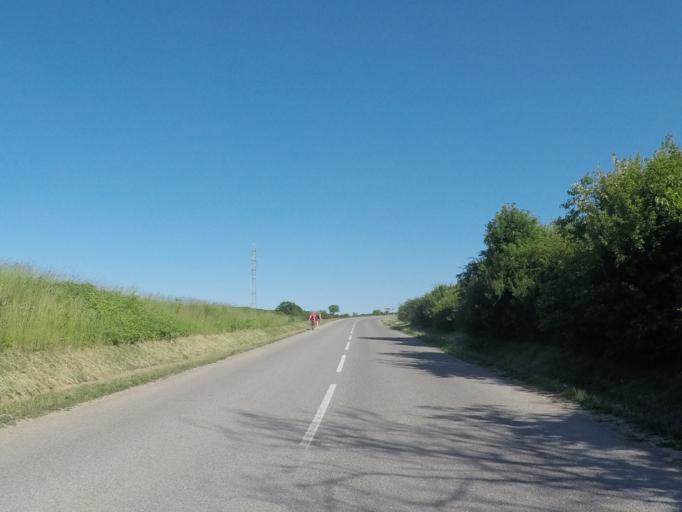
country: SK
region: Kosicky
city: Roznava
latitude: 48.5364
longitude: 20.4095
